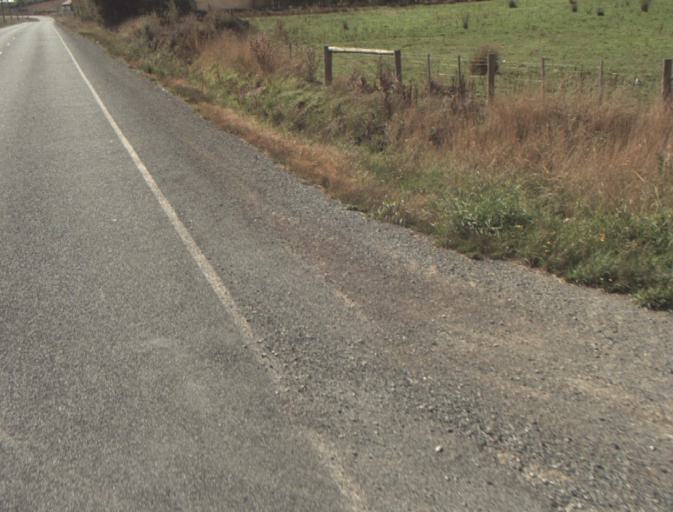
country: AU
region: Tasmania
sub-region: Launceston
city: Mayfield
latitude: -41.2417
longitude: 147.2163
